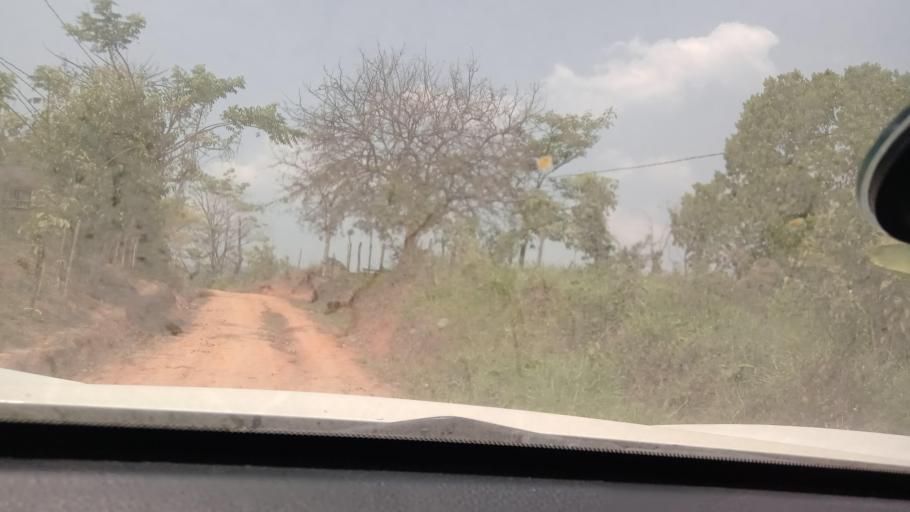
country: MX
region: Chiapas
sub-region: Tecpatan
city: Raudales Malpaso
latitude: 17.4688
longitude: -93.8256
